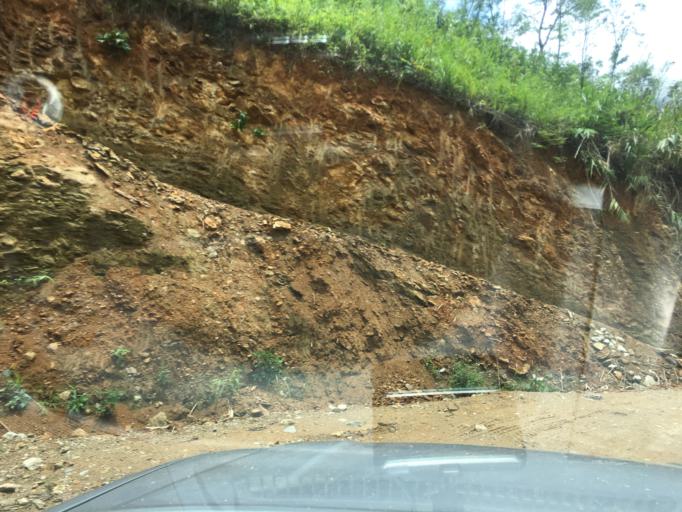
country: VN
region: Yen Bai
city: Son Thinh
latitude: 21.6770
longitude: 104.5400
